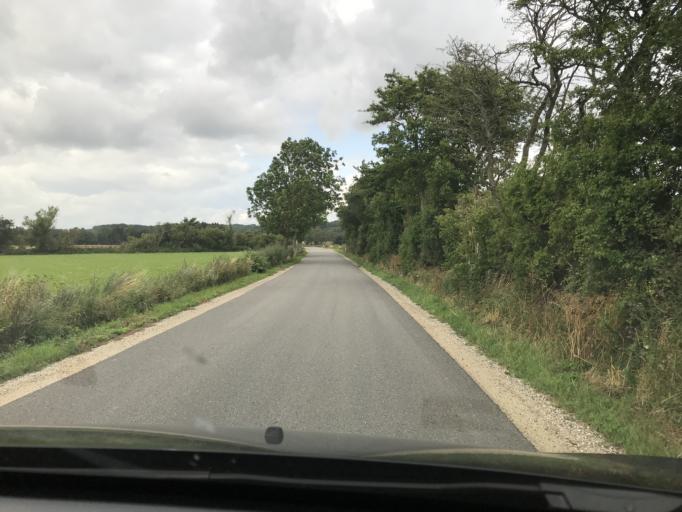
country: DK
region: Central Jutland
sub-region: Syddjurs Kommune
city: Ryomgard
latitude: 56.3780
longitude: 10.4319
